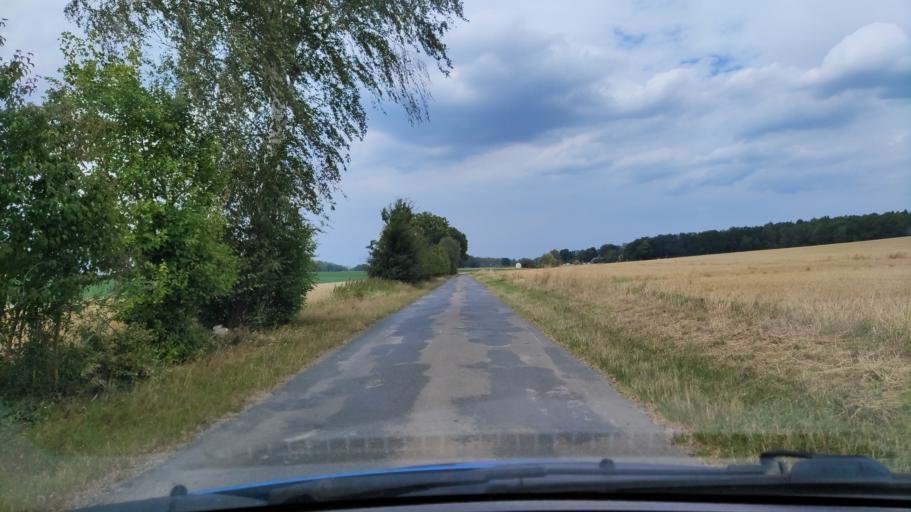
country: DE
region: Lower Saxony
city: Schnega
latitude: 52.9323
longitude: 10.8803
